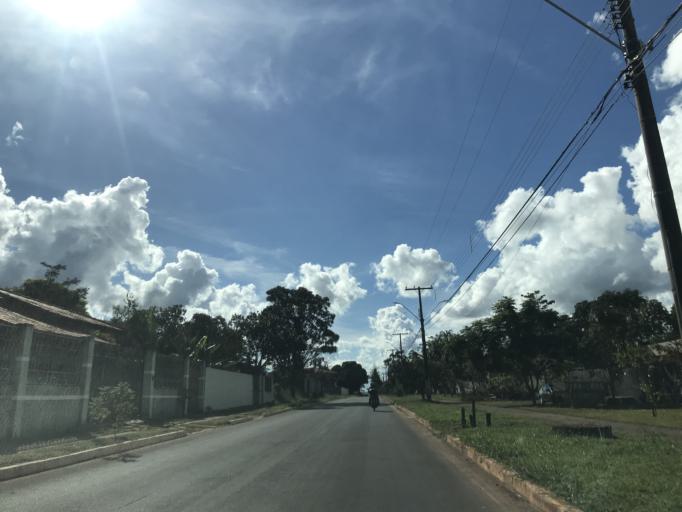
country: BR
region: Federal District
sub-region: Brasilia
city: Brasilia
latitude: -15.7454
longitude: -47.7516
